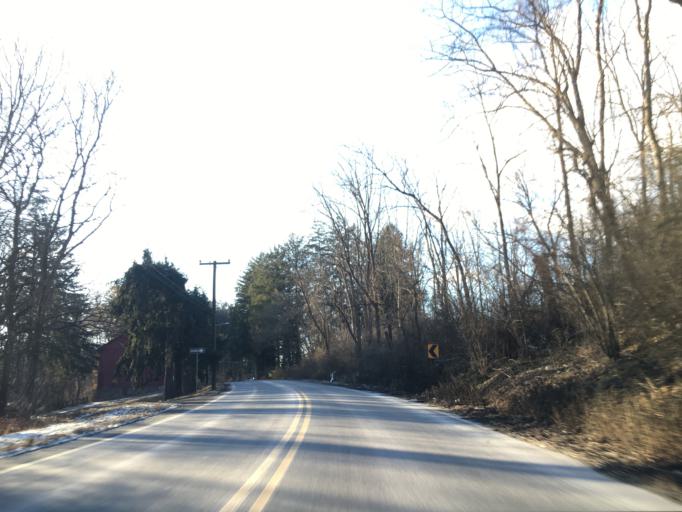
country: US
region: Pennsylvania
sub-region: Lehigh County
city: Egypt
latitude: 40.6739
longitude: -75.5204
